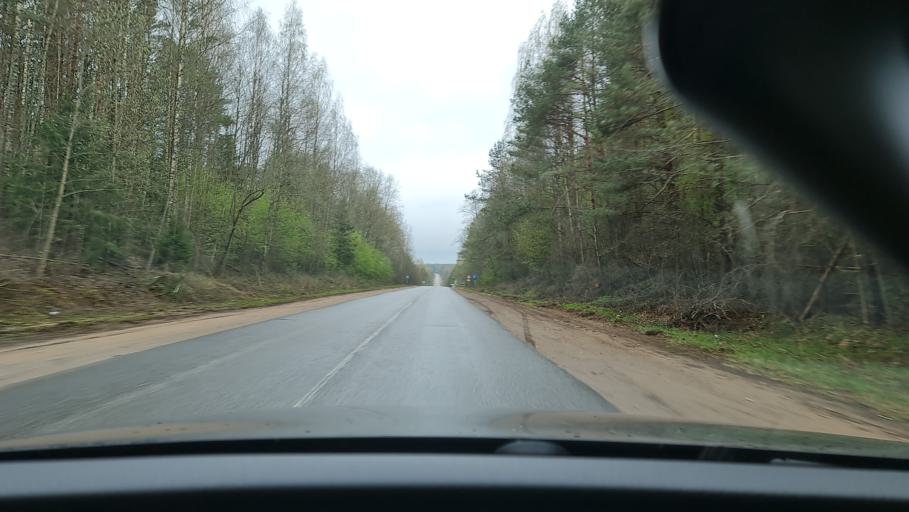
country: RU
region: Novgorod
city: Demyansk
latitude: 57.6606
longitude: 32.5174
